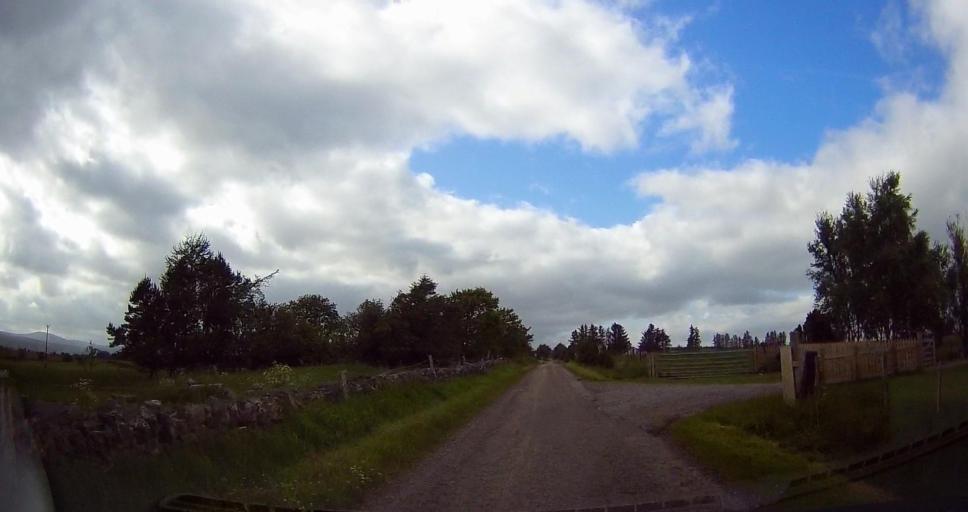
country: GB
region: Scotland
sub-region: Highland
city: Alness
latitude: 58.0726
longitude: -4.4358
